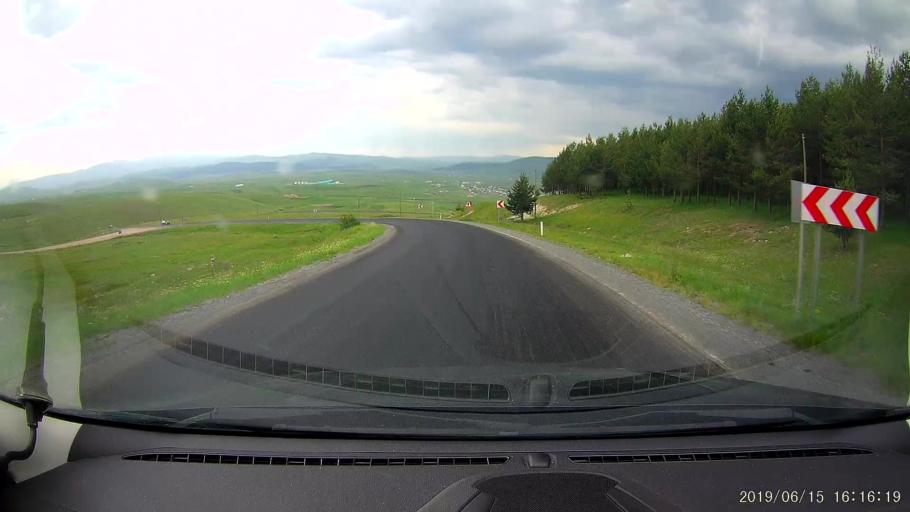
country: TR
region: Ardahan
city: Hanak
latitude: 41.2598
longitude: 42.8524
